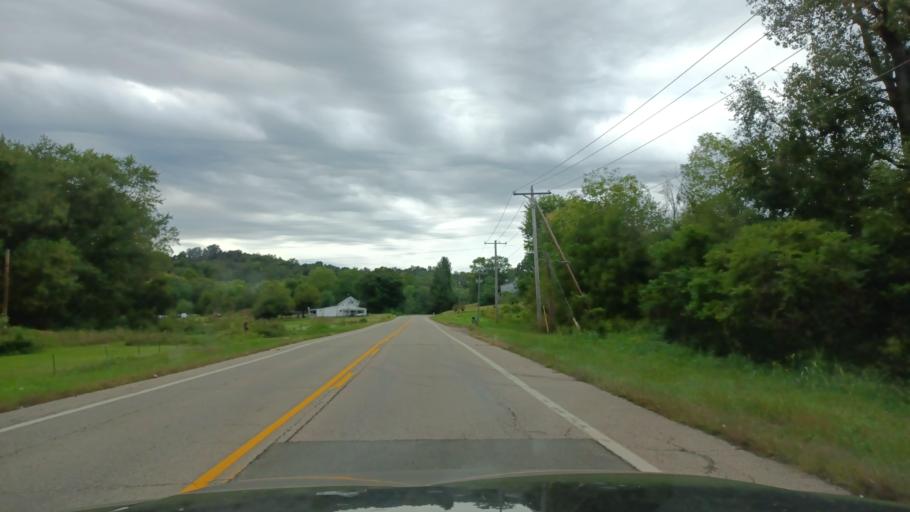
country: US
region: Ohio
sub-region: Vinton County
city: McArthur
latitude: 39.2351
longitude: -82.4433
